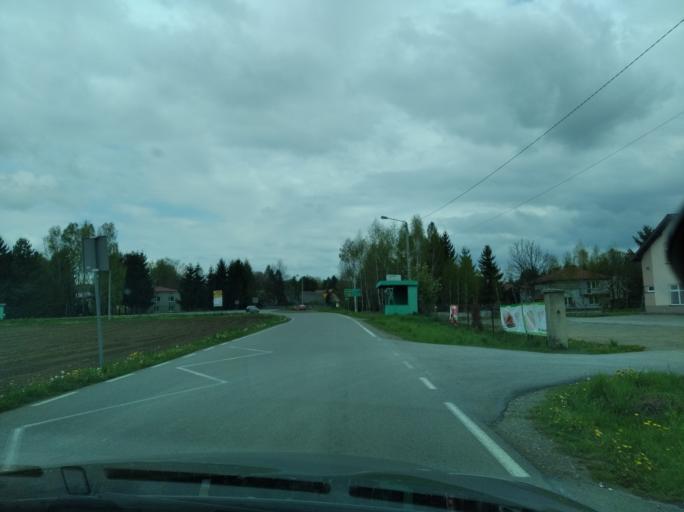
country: PL
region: Subcarpathian Voivodeship
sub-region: Powiat brzozowski
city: Turze Pole
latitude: 49.6575
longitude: 21.9961
